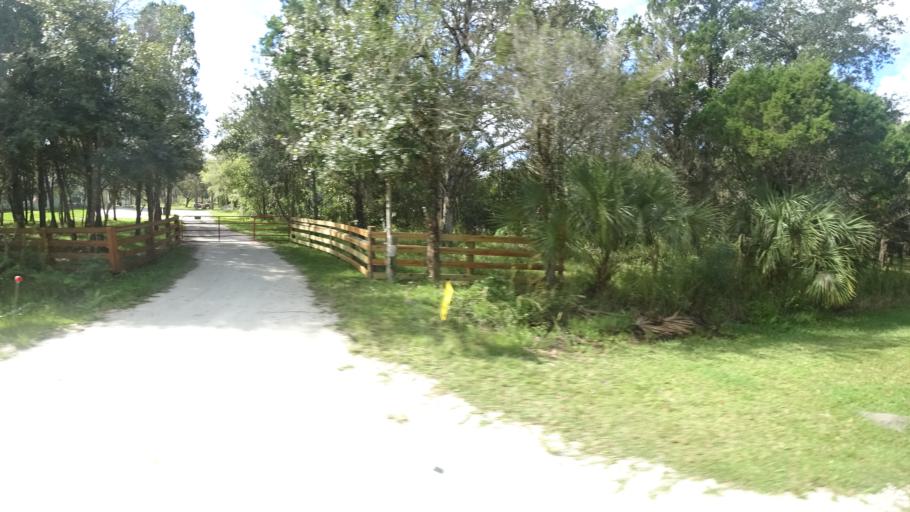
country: US
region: Florida
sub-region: Sarasota County
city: Lake Sarasota
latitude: 27.3438
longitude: -82.2120
